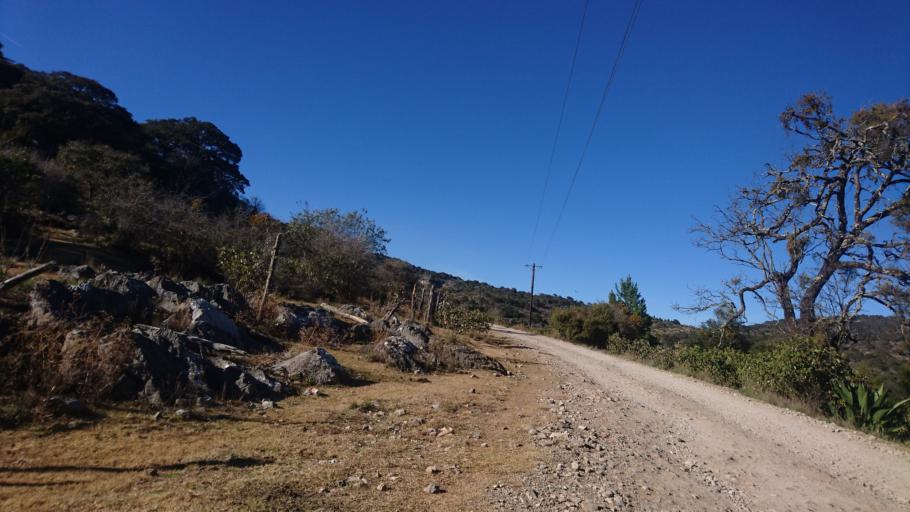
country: MX
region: San Luis Potosi
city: Zaragoza
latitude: 22.0291
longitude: -100.6034
